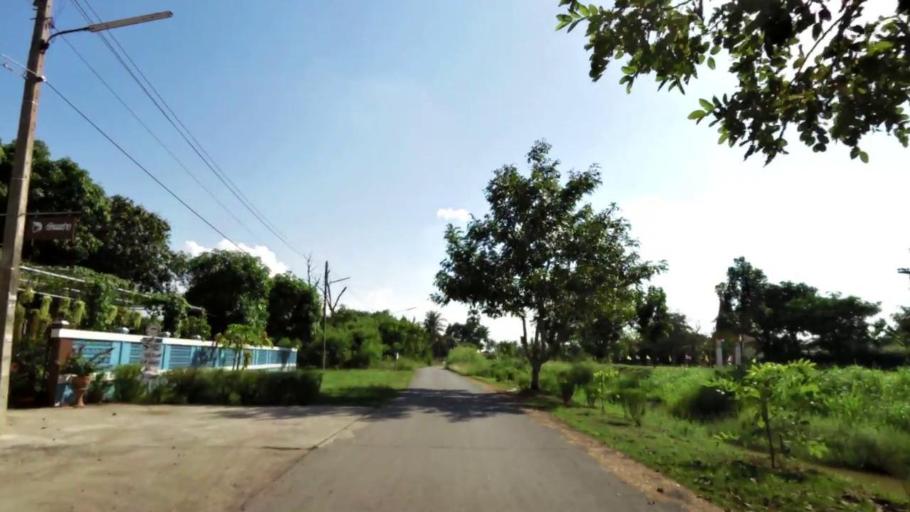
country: TH
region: Ang Thong
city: Ang Thong
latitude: 14.5904
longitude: 100.4694
